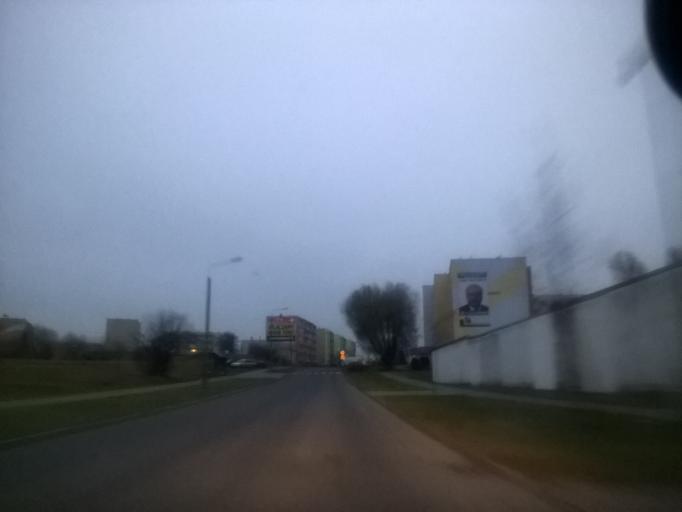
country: PL
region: Warmian-Masurian Voivodeship
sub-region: Powiat ketrzynski
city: Ketrzyn
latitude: 54.0931
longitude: 21.3769
